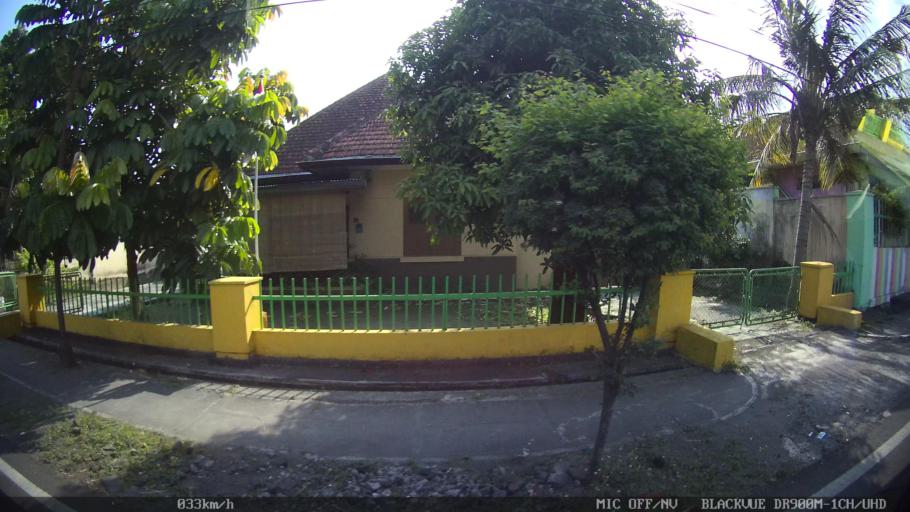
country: ID
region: Daerah Istimewa Yogyakarta
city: Kasihan
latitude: -7.8300
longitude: 110.3442
